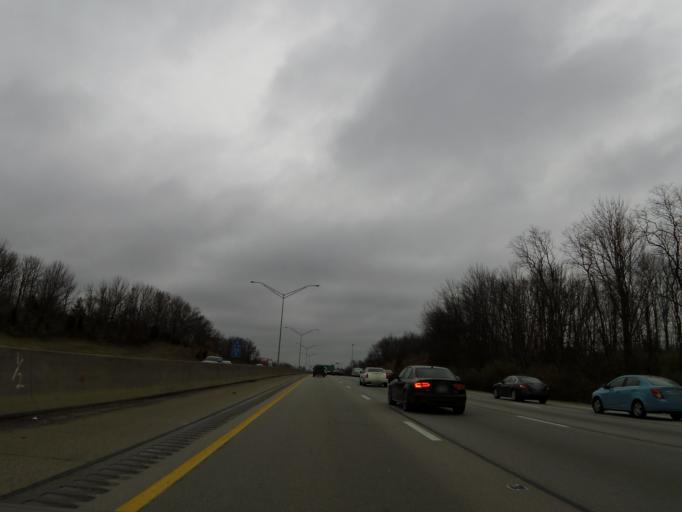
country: US
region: Kentucky
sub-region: Boone County
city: Walton
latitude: 38.8841
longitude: -84.6258
